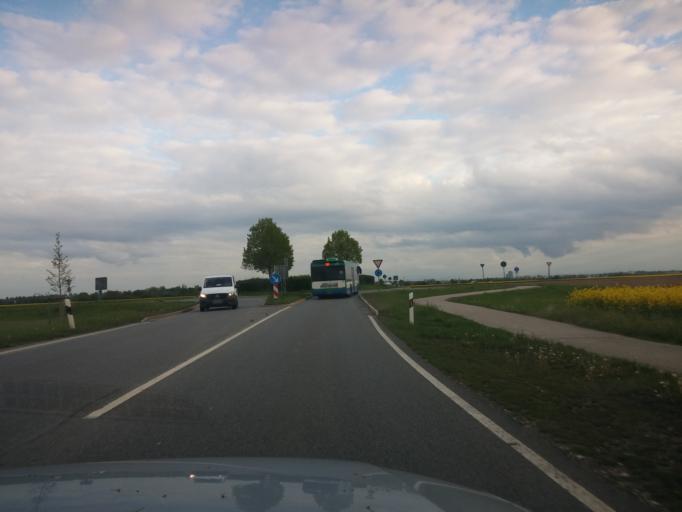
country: DE
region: Bavaria
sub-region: Upper Bavaria
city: Feldkirchen
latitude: 48.1395
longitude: 11.7361
